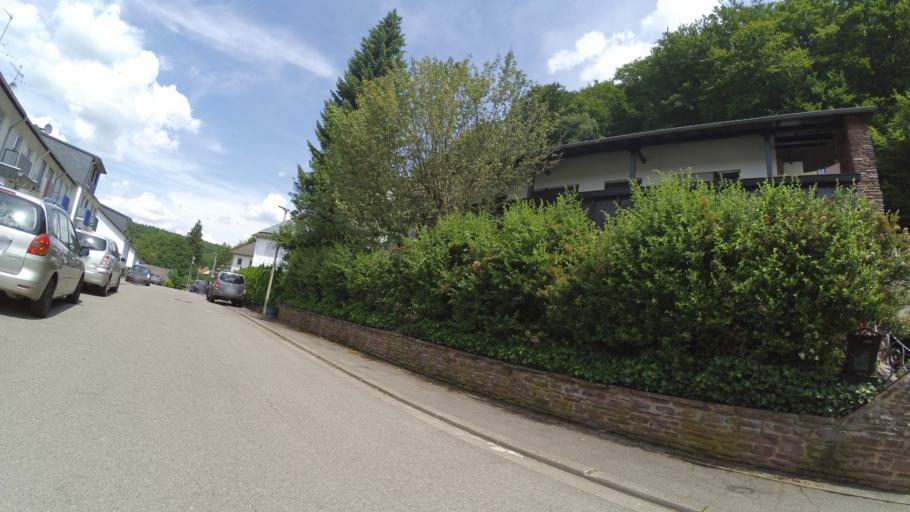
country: DE
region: Rheinland-Pfalz
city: Grossbundenbach
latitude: 49.3057
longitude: 7.3773
